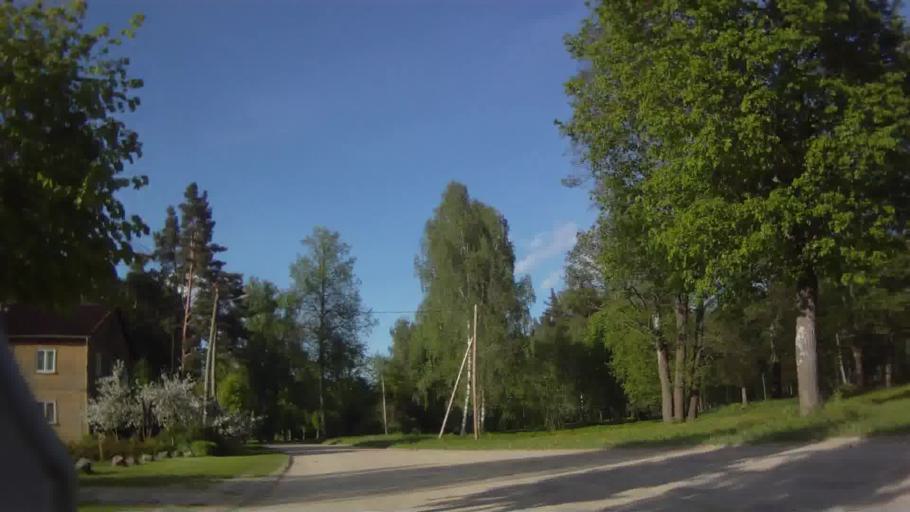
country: LV
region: Baldone
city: Baldone
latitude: 56.7433
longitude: 24.4053
